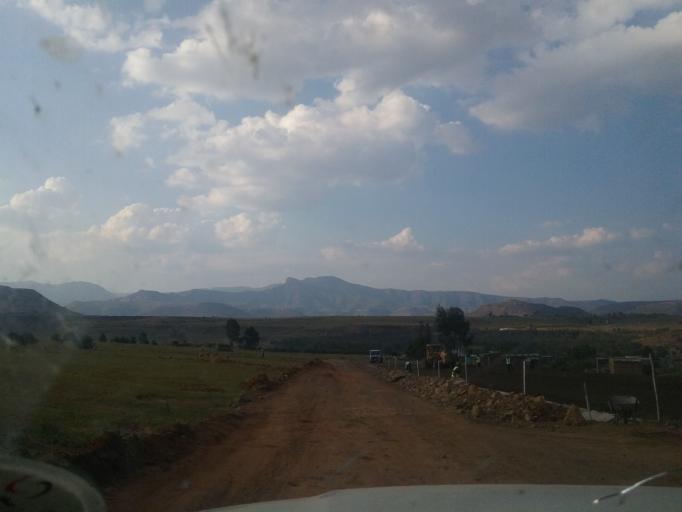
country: LS
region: Quthing
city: Quthing
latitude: -30.3986
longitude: 27.6118
